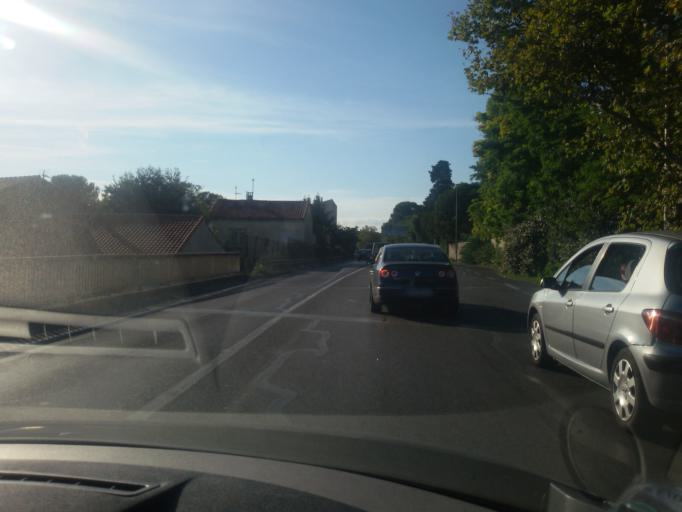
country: FR
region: Languedoc-Roussillon
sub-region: Departement de l'Herault
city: Montpellier
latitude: 43.5987
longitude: 3.8727
